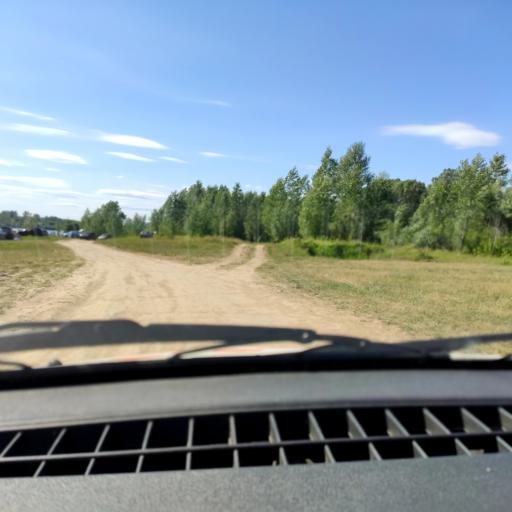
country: RU
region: Bashkortostan
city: Iglino
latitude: 54.7996
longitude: 56.2266
